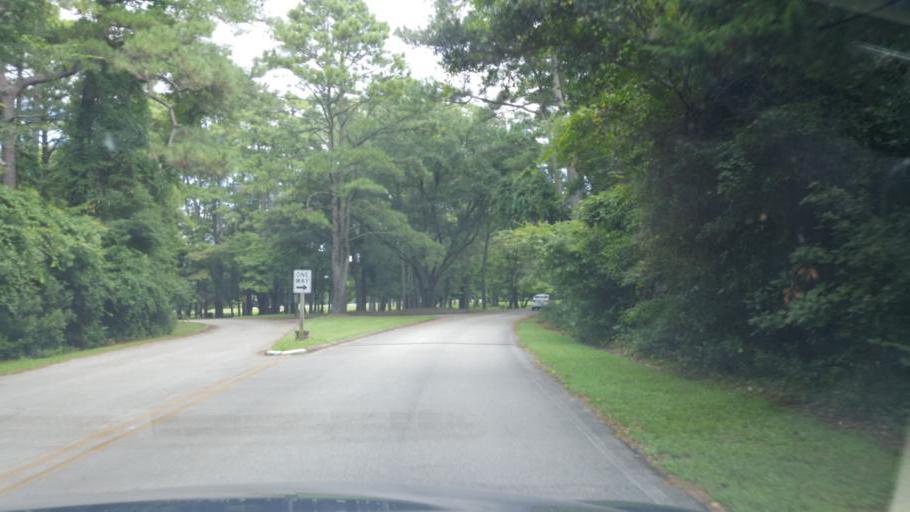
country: US
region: North Carolina
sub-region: Dare County
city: Manteo
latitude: 35.9352
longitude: -75.7082
